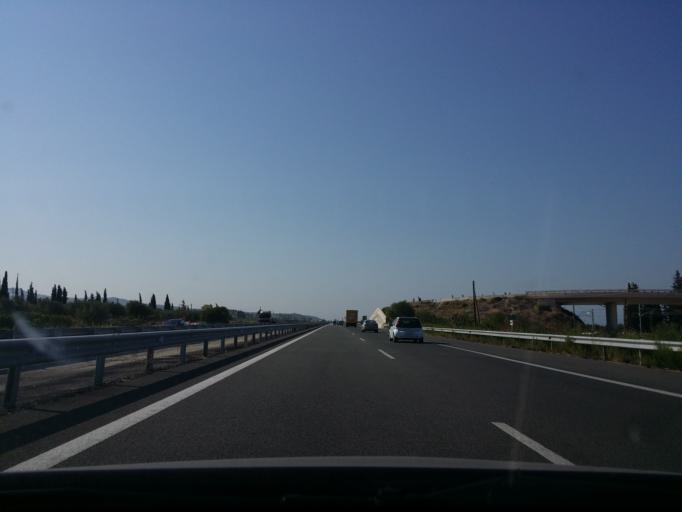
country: GR
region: Peloponnese
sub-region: Nomos Korinthias
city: Velo
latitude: 37.9511
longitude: 22.7551
